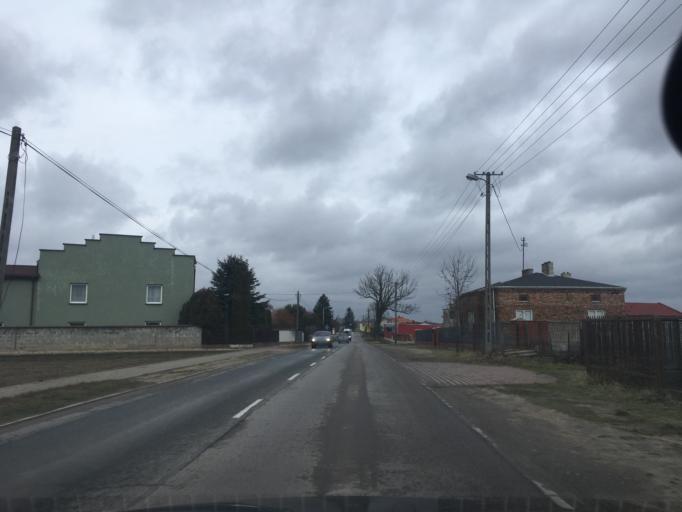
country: PL
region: Masovian Voivodeship
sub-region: Powiat piaseczynski
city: Lesznowola
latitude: 52.1055
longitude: 20.9313
